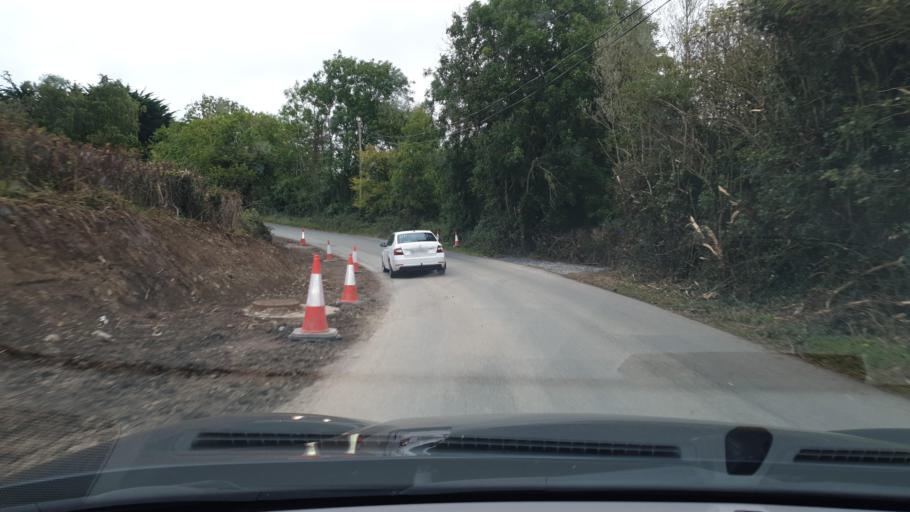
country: IE
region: Leinster
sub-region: An Mhi
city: Dunshaughlin
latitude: 53.5188
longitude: -6.5394
